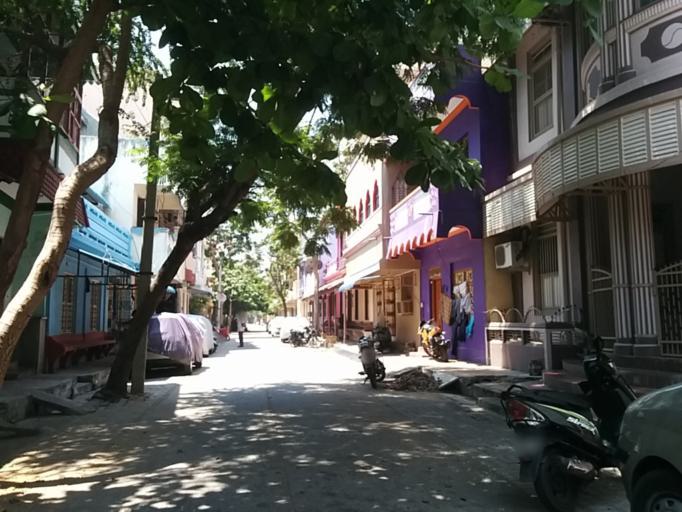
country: IN
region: Pondicherry
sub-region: Puducherry
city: Puducherry
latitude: 11.9274
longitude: 79.8303
